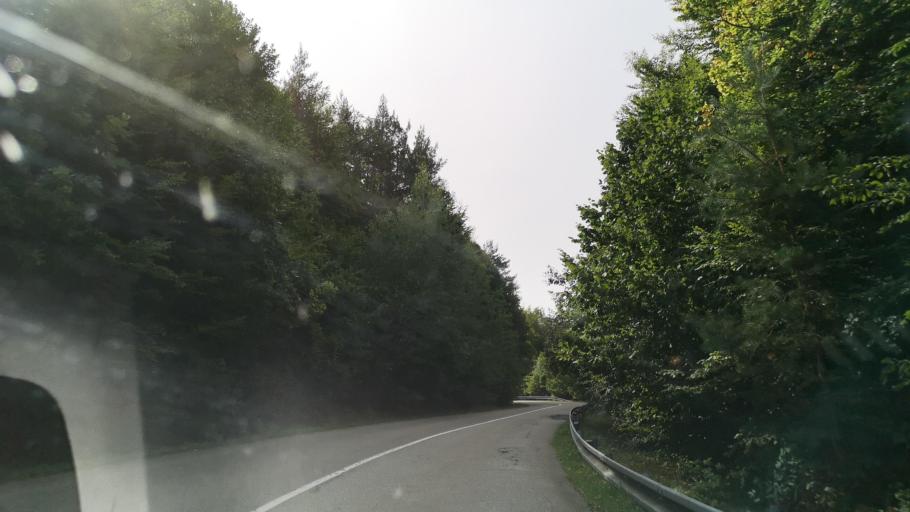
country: SK
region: Banskobystricky
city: Revuca
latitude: 48.5881
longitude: 20.0512
